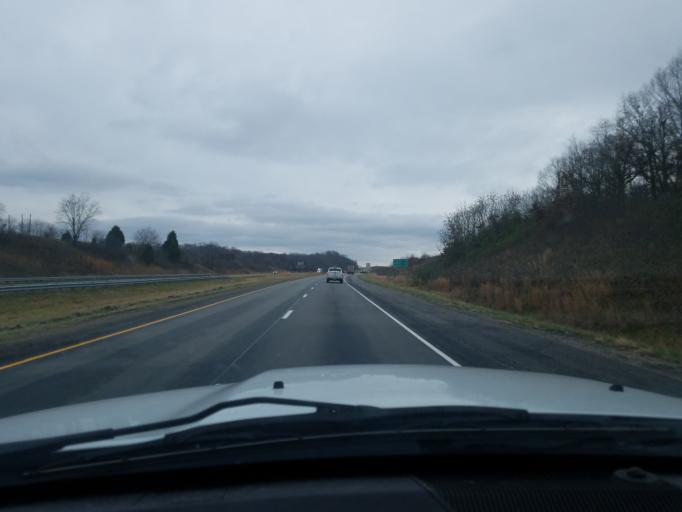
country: US
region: Indiana
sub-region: Dubois County
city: Ferdinand
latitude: 38.2048
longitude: -86.8493
